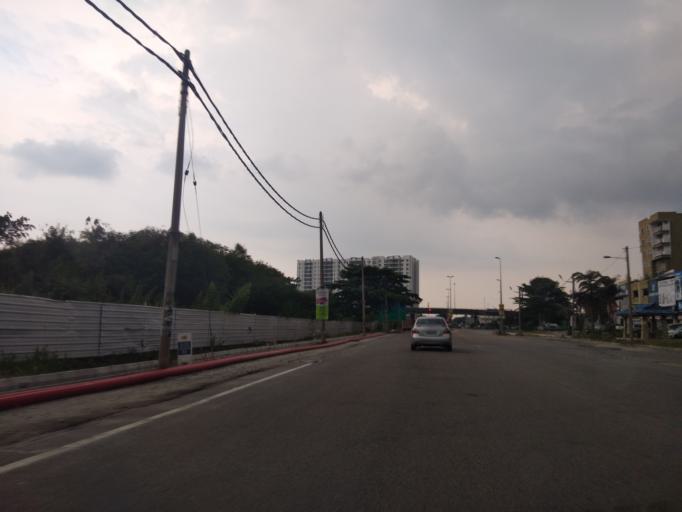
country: MY
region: Penang
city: Permatang Kuching
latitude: 5.4405
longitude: 100.3814
